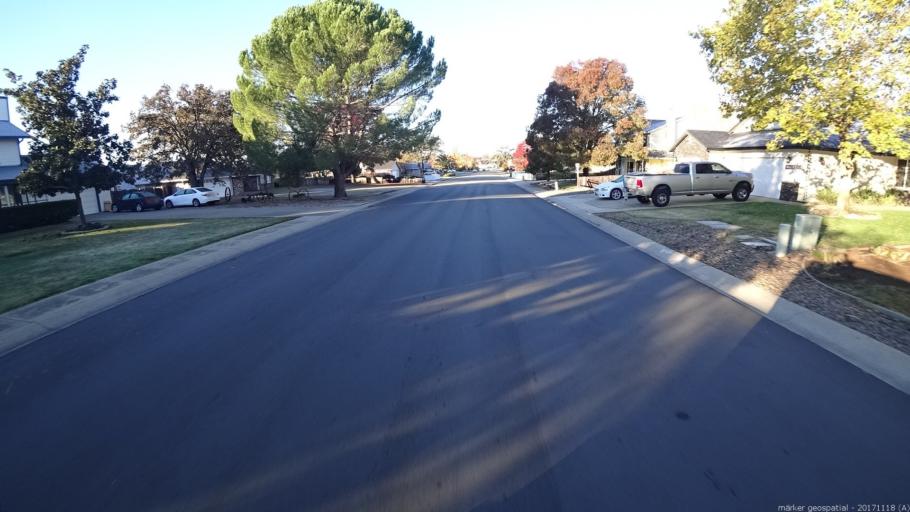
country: US
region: California
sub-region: Shasta County
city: Cottonwood
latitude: 40.3973
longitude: -122.2914
